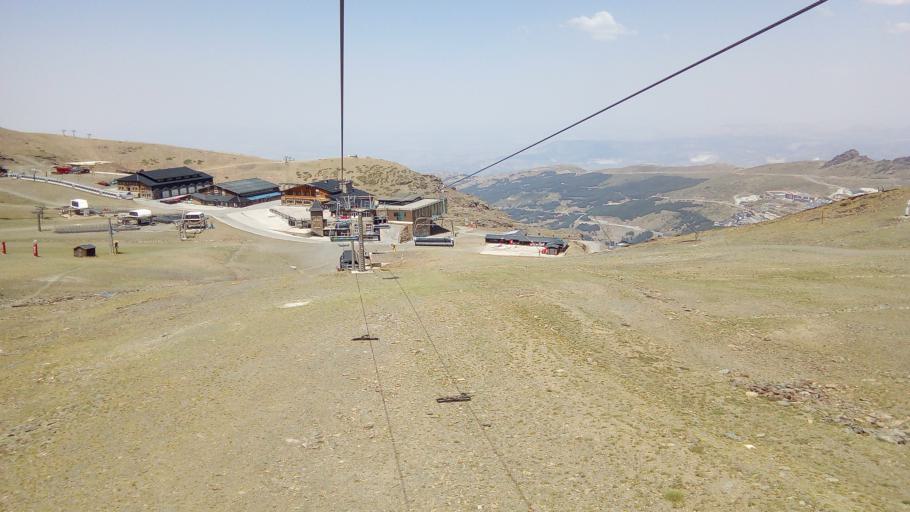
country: ES
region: Andalusia
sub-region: Provincia de Granada
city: Guejar-Sierra
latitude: 37.0694
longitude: -3.3847
